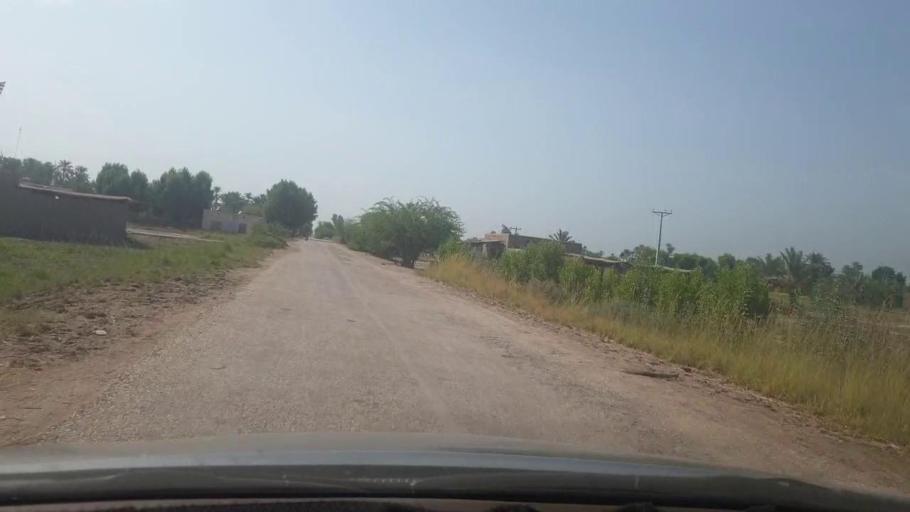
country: PK
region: Sindh
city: Gambat
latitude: 27.3207
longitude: 68.5558
